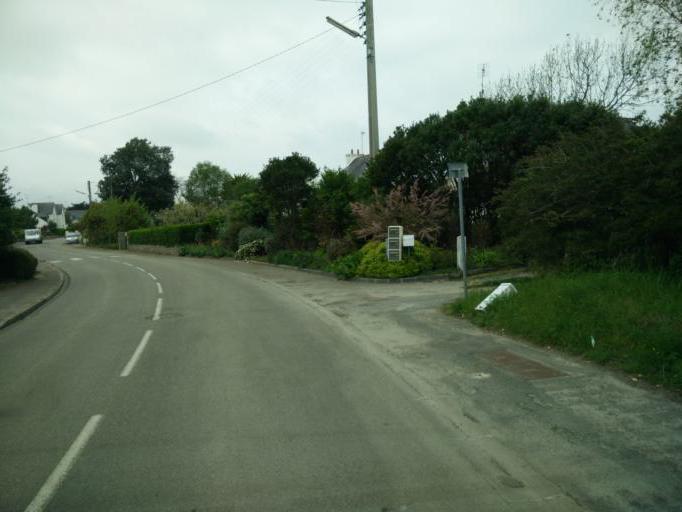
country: FR
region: Brittany
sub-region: Departement du Finistere
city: Loctudy
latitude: 47.8236
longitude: -4.1638
